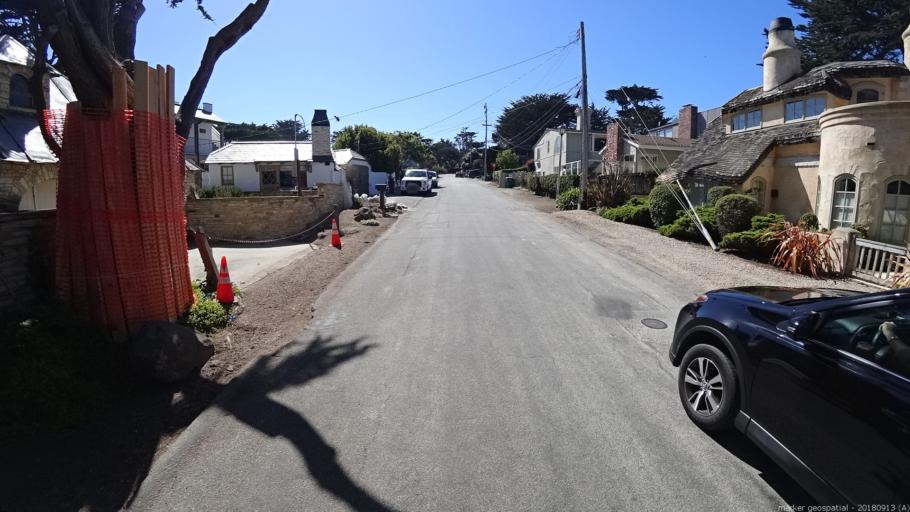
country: US
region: California
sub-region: Monterey County
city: Carmel-by-the-Sea
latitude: 36.5446
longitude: -121.9304
